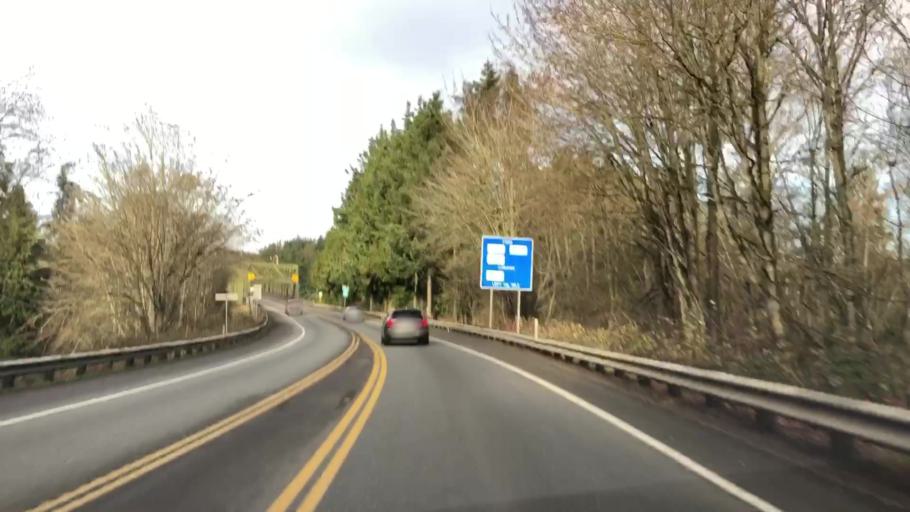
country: US
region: Washington
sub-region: Kitsap County
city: Suquamish
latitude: 47.7109
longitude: -122.5620
